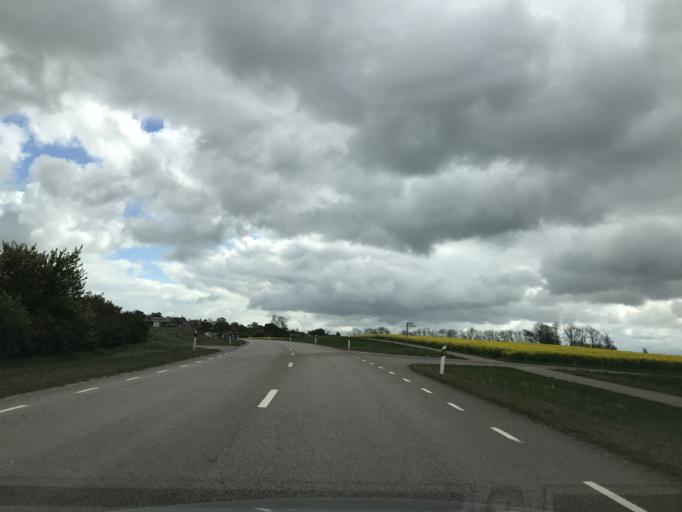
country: SE
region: Skane
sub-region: Helsingborg
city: Glumslov
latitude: 55.9525
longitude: 12.7965
